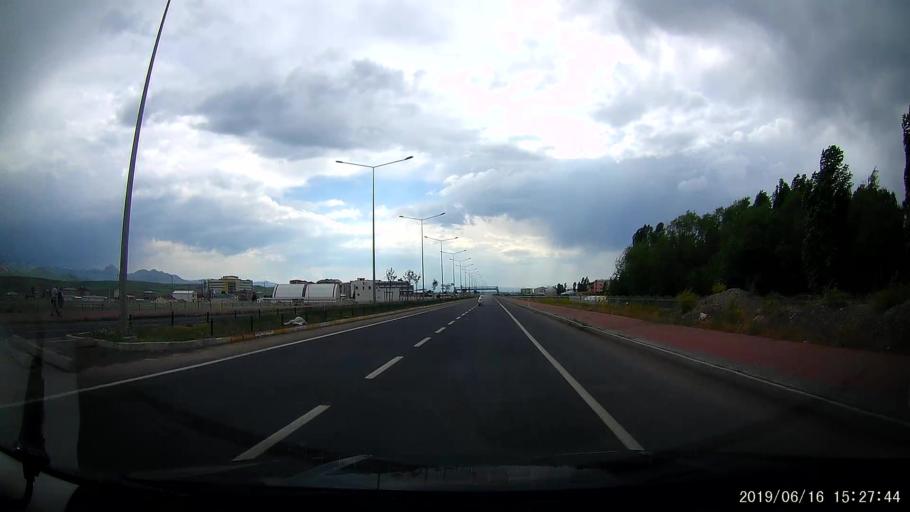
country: TR
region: Erzurum
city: Horasan
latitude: 40.0337
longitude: 42.1537
